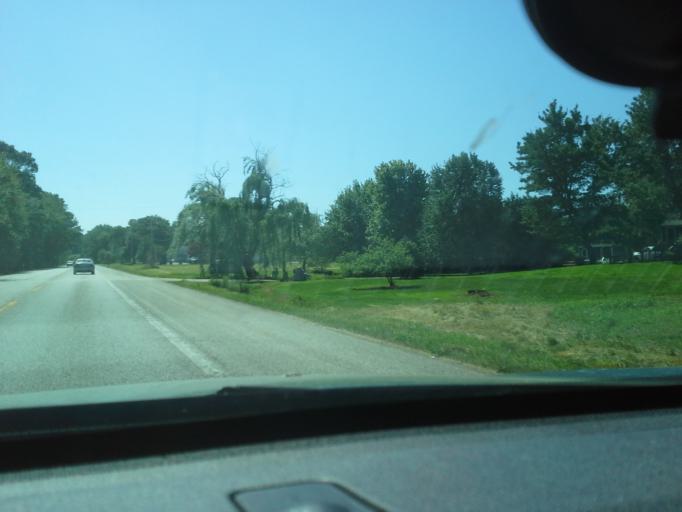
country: US
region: Maryland
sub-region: Anne Arundel County
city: Deale
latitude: 38.7933
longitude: -76.5640
